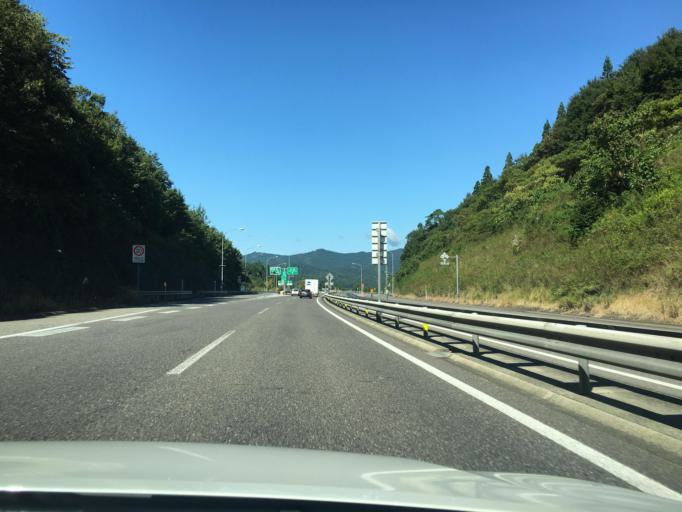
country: JP
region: Fukushima
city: Kitakata
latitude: 37.5729
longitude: 139.6546
